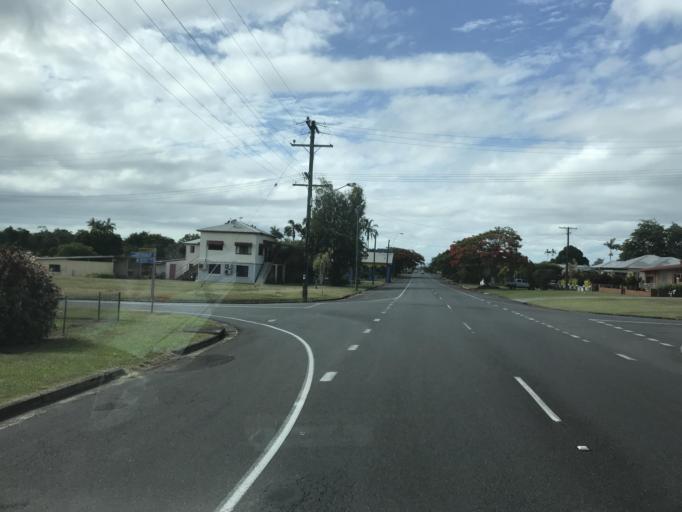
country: AU
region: Queensland
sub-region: Cassowary Coast
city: Innisfail
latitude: -17.5388
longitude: 146.0328
